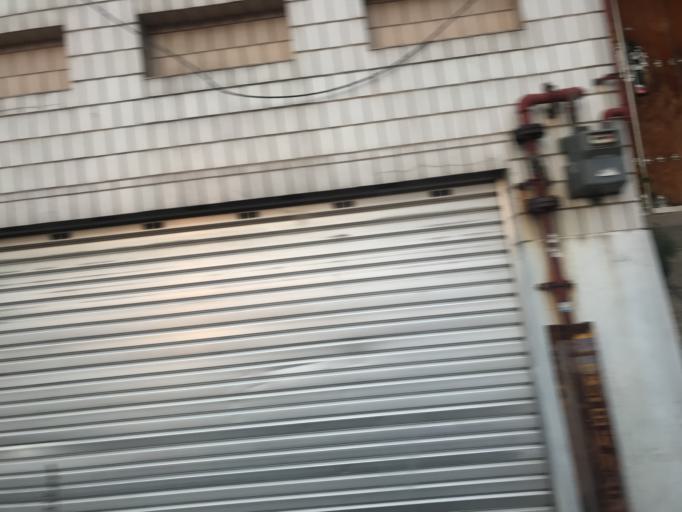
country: KR
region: Seoul
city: Seoul
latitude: 37.5821
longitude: 126.9821
